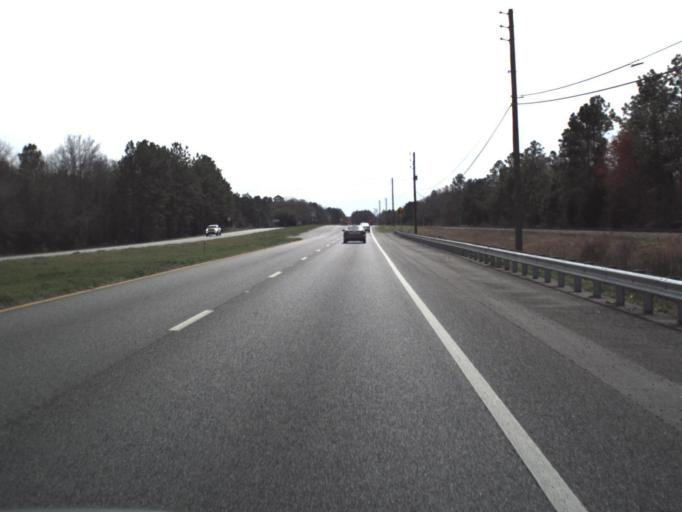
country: US
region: Florida
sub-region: Washington County
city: Chipley
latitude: 30.7142
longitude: -85.3907
